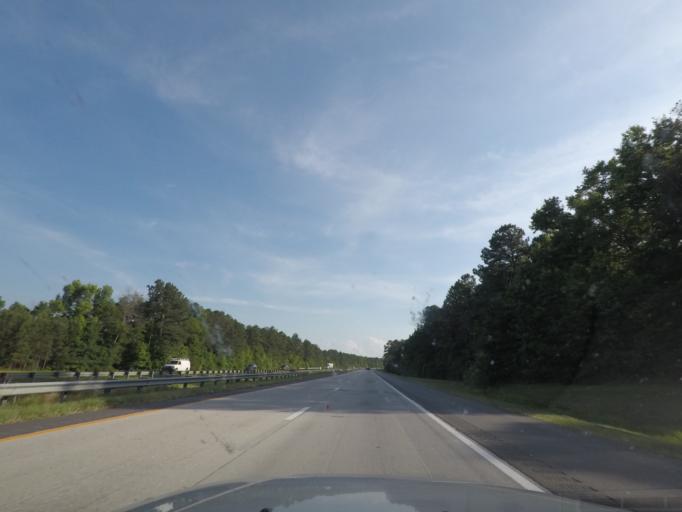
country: US
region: North Carolina
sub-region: Granville County
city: Oxford
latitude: 36.2558
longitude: -78.6198
